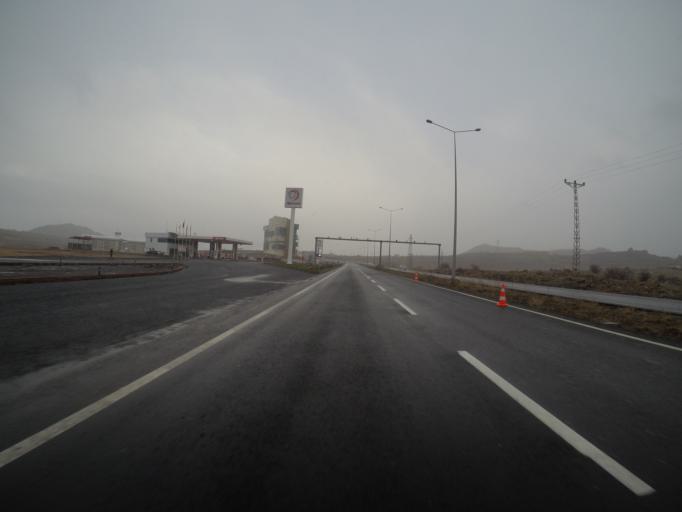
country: TR
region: Nevsehir
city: Nevsehir
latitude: 38.6730
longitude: 34.7532
